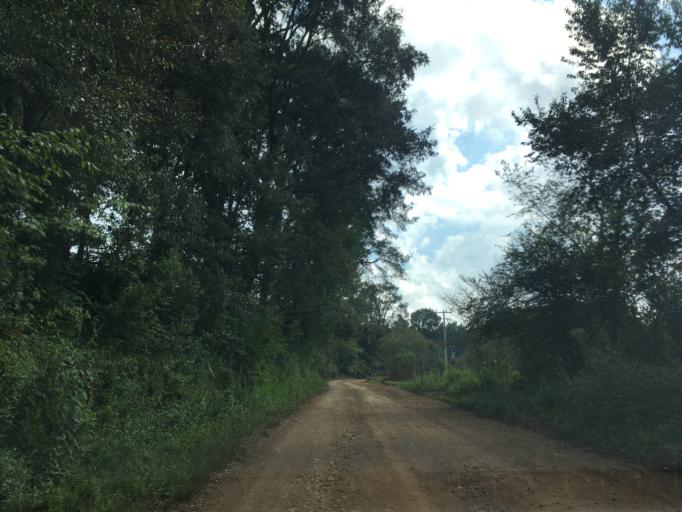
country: MX
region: Michoacan
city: Acuitzio del Canje
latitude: 19.5161
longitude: -101.2112
